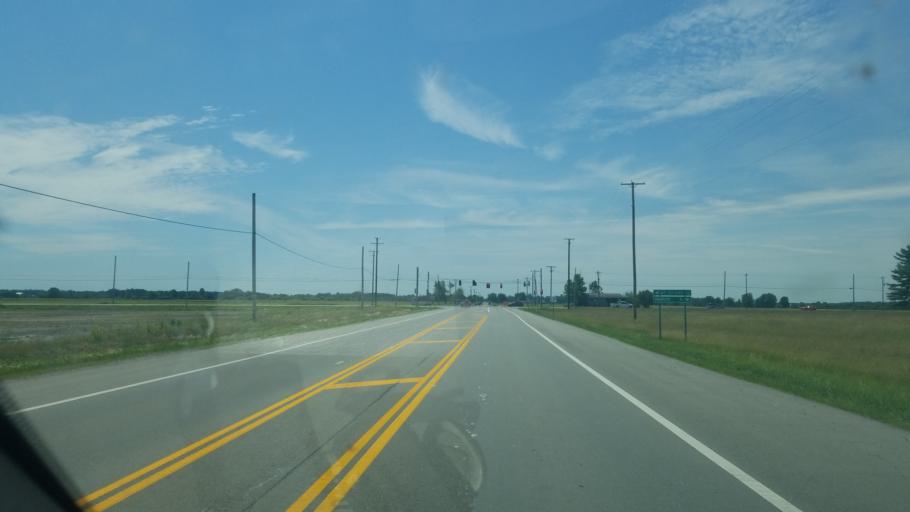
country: US
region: Ohio
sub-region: Marion County
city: Marion
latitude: 40.5837
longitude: -83.0397
